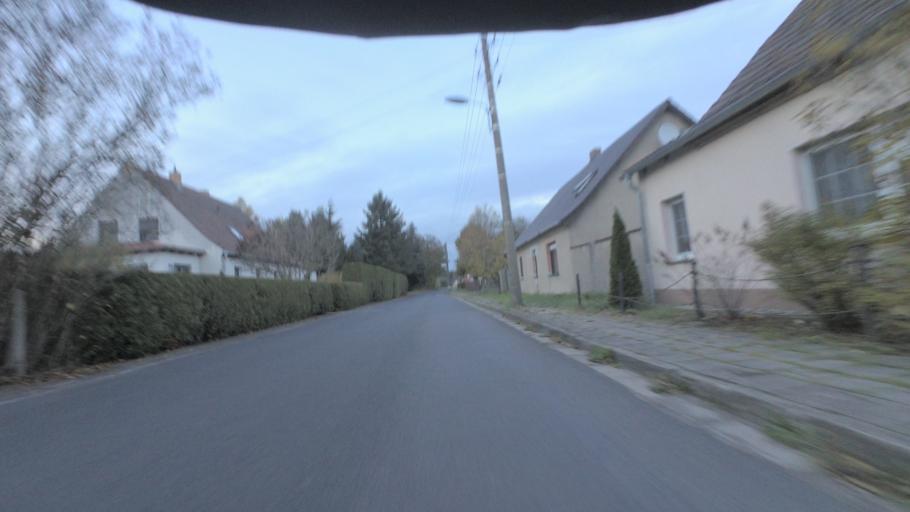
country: DE
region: Brandenburg
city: Sonnewalde
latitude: 51.7711
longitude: 13.6180
